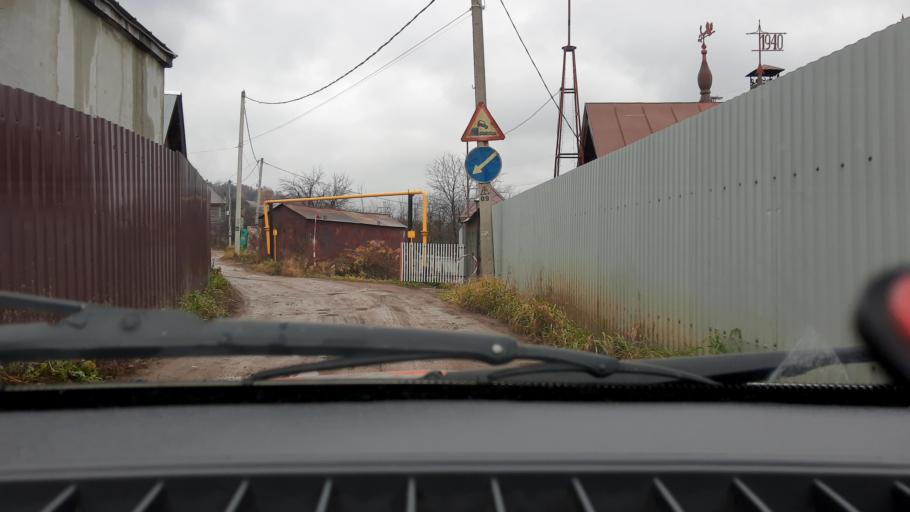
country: RU
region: Bashkortostan
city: Ufa
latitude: 54.8306
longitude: 56.0614
